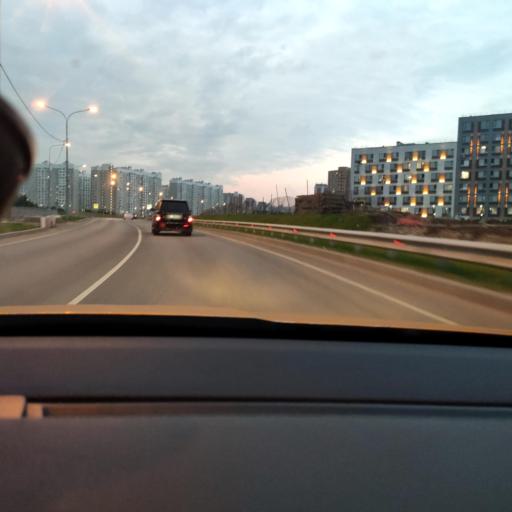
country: RU
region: Moskovskaya
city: Vidnoye
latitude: 55.5341
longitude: 37.7128
